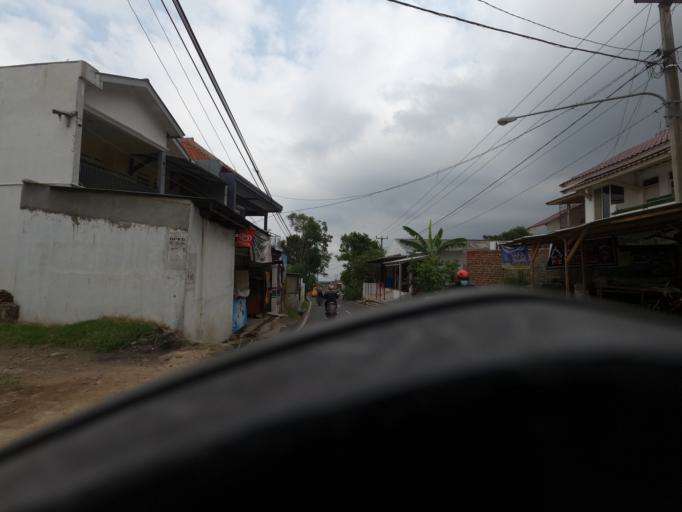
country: ID
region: West Java
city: Cimahi
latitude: -6.8227
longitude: 107.5331
